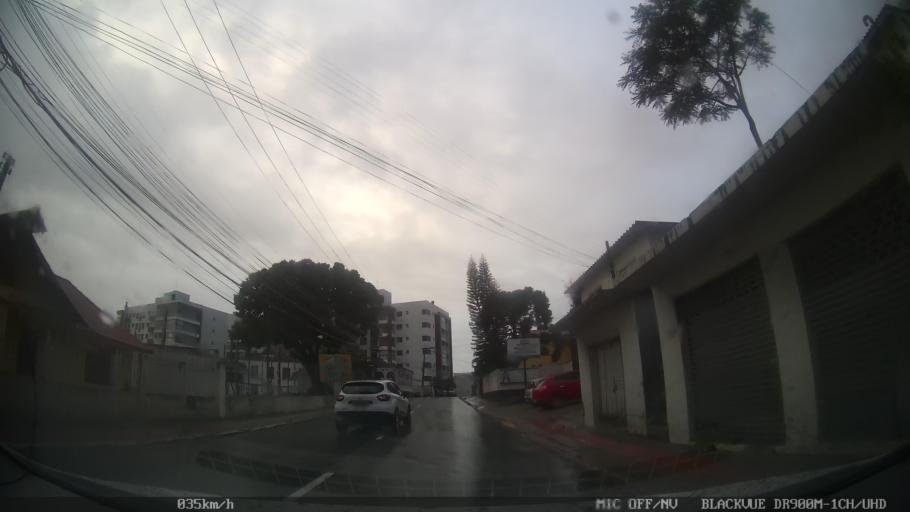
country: BR
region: Santa Catarina
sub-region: Sao Jose
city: Campinas
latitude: -27.6115
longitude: -48.6277
